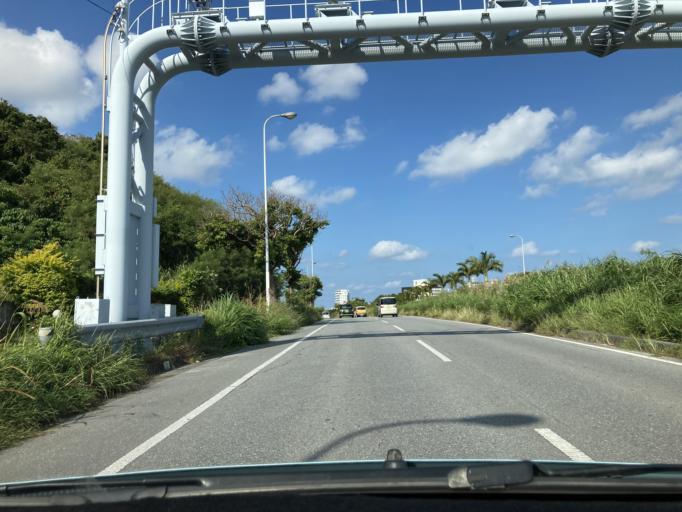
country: JP
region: Okinawa
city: Tomigusuku
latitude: 26.1927
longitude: 127.7001
